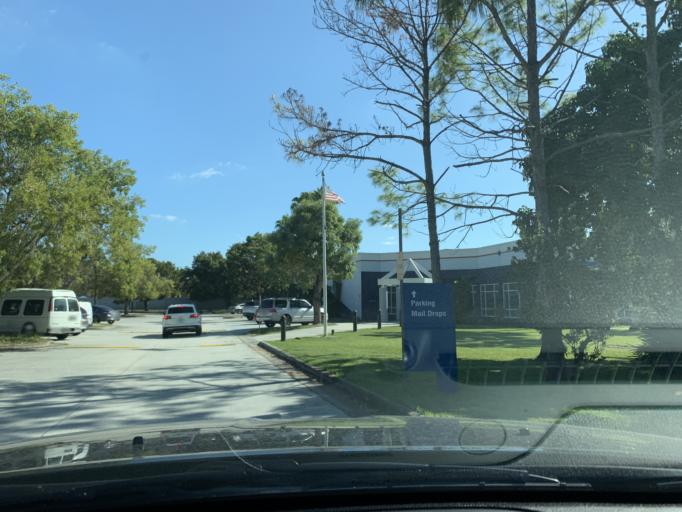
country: US
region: Florida
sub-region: Miami-Dade County
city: Country Walk
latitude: 25.6251
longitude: -80.4126
